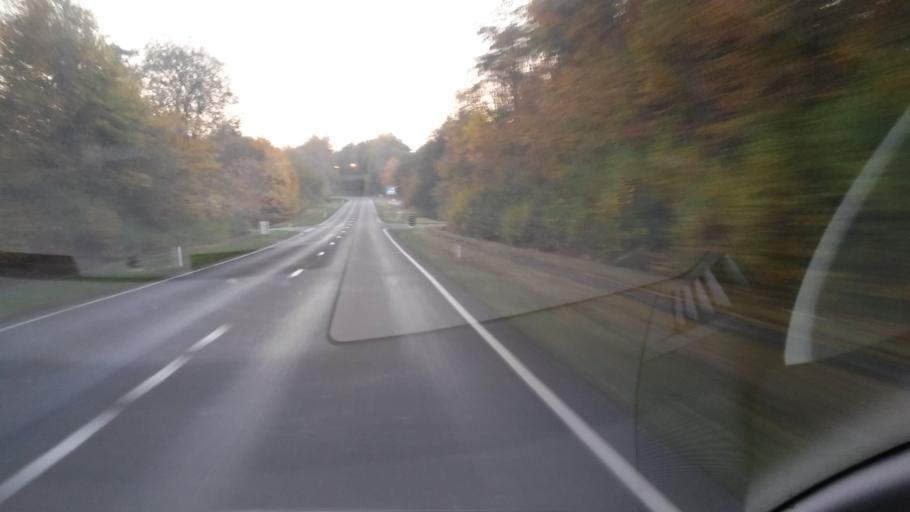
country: BE
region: Wallonia
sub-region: Province du Luxembourg
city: Etalle
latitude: 49.6756
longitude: 5.6118
